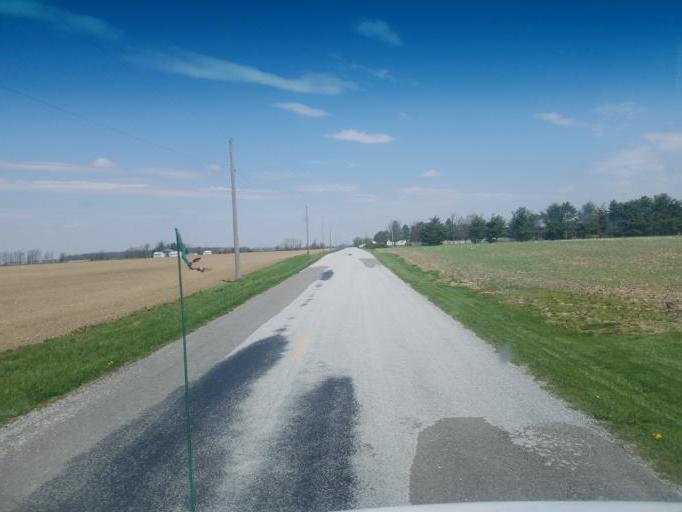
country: US
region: Ohio
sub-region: Hardin County
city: Forest
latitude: 40.7512
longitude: -83.5378
